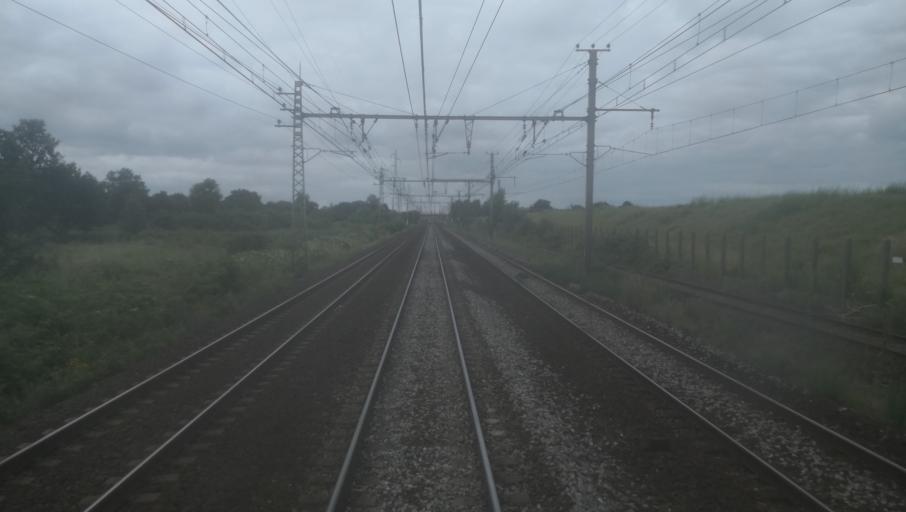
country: FR
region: Midi-Pyrenees
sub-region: Departement de la Haute-Garonne
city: Fenouillet
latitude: 43.6795
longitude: 1.4043
